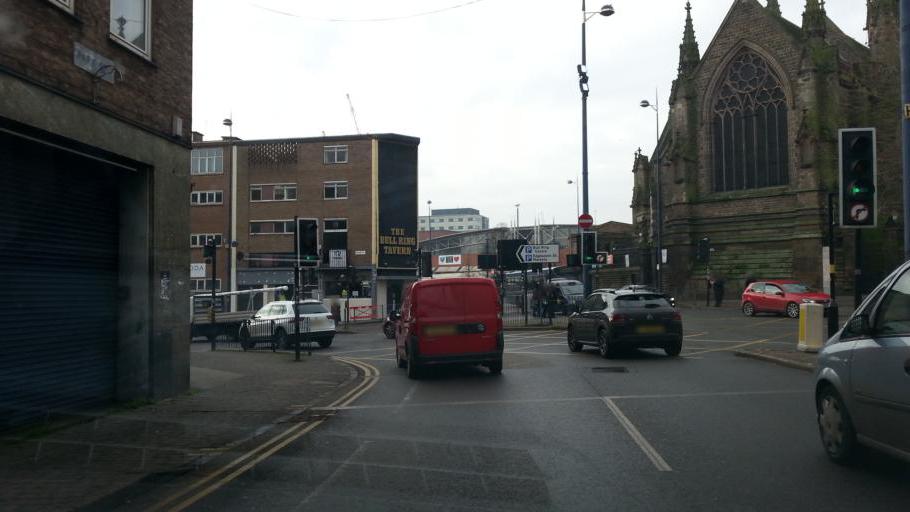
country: GB
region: England
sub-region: City and Borough of Birmingham
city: Birmingham
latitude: 52.4773
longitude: -1.8923
